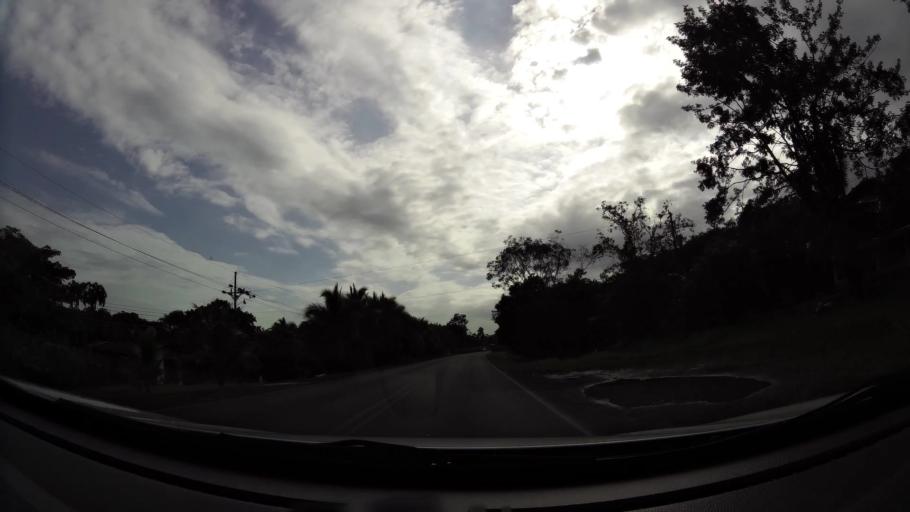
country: CR
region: Limon
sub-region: Canton de Guacimo
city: Guacimo
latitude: 10.1957
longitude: -83.6466
